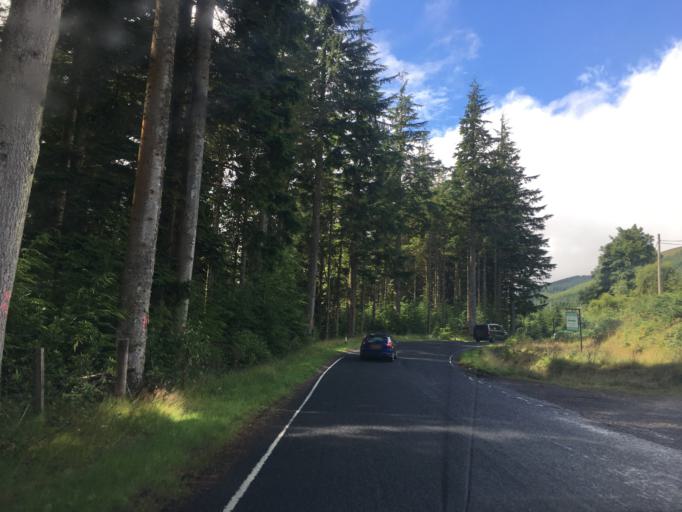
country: GB
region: Scotland
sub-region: Argyll and Bute
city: Dunoon
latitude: 55.9888
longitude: -4.9961
